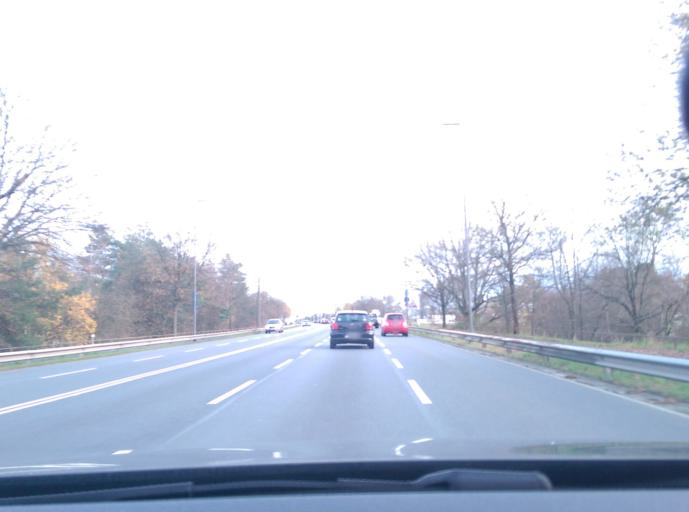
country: DE
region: Lower Saxony
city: Celle
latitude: 52.6078
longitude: 10.0514
